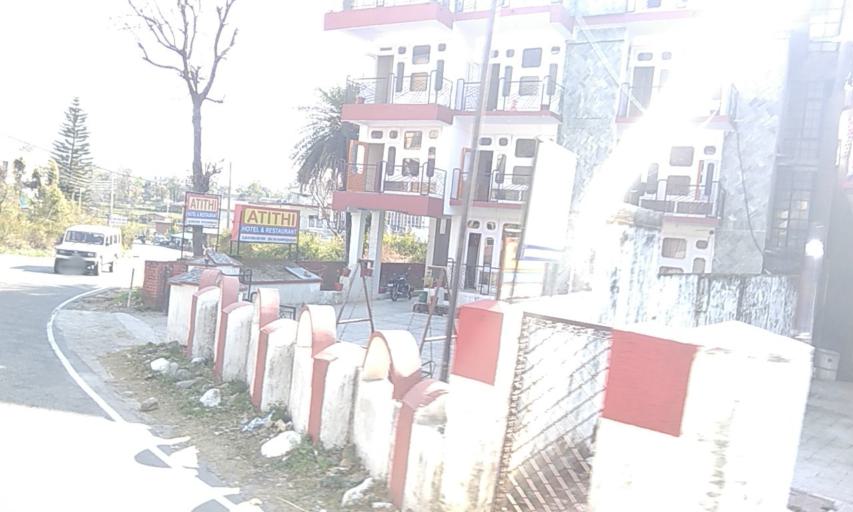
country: IN
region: Himachal Pradesh
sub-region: Kangra
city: Dharmsala
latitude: 32.1547
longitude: 76.4163
